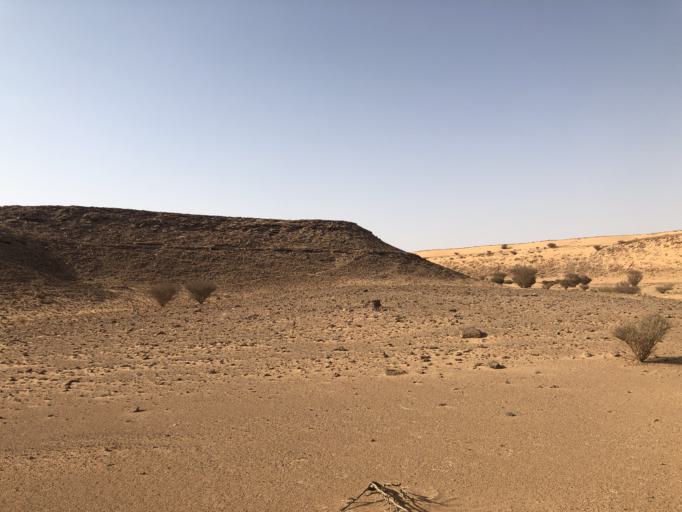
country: SA
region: Ar Riyad
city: shokhaib
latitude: 23.6256
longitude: 46.0903
